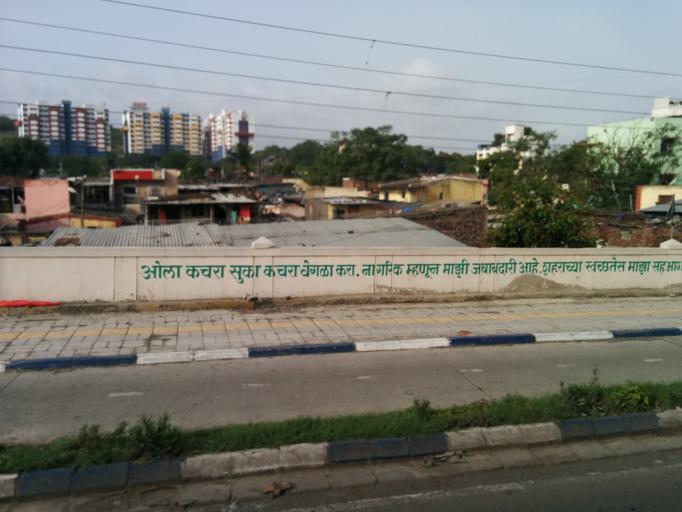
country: IN
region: Maharashtra
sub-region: Pune Division
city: Pune
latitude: 18.5059
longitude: 73.9144
